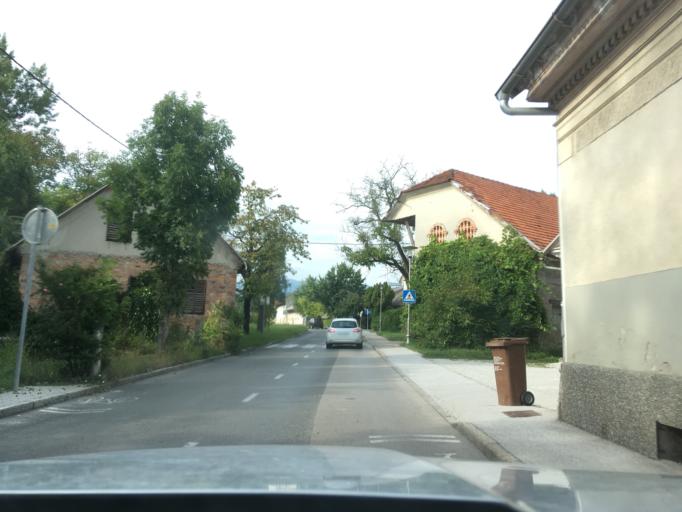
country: SI
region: Domzale
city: Radomlje
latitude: 46.1746
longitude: 14.6100
